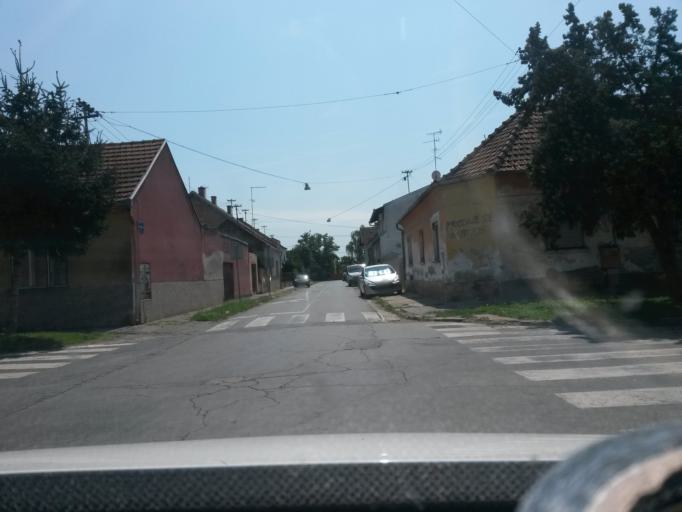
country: HR
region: Osjecko-Baranjska
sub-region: Grad Osijek
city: Osijek
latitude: 45.5581
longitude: 18.6585
